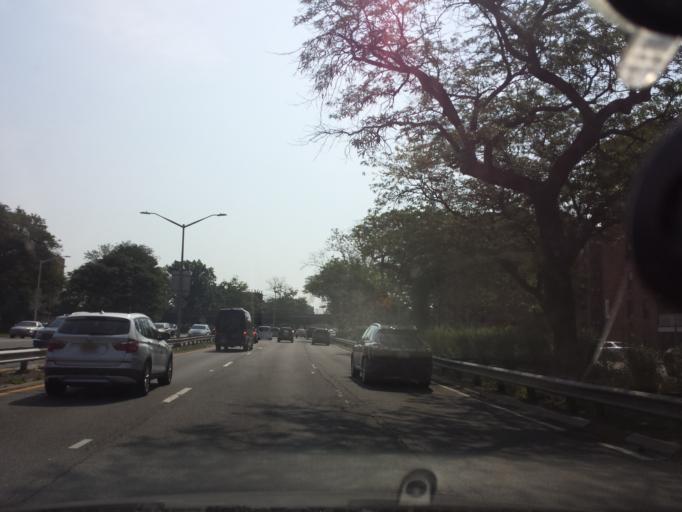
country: US
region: New York
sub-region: Kings County
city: Coney Island
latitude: 40.5850
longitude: -73.9573
